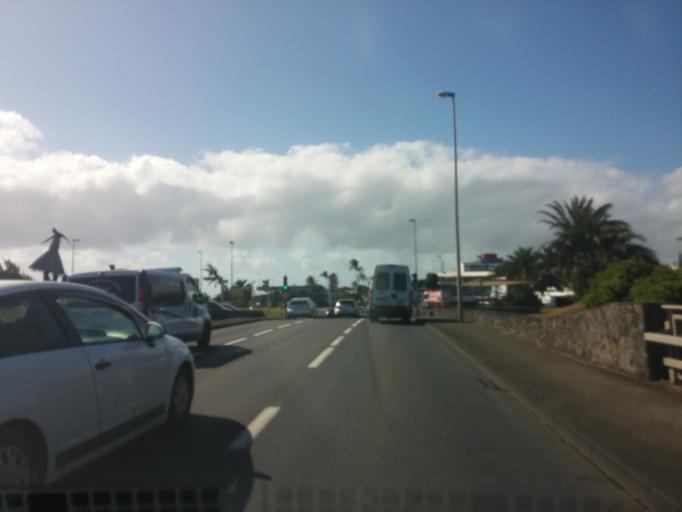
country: RE
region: Reunion
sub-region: Reunion
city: Saint-Denis
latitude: -20.8860
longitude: 55.4730
